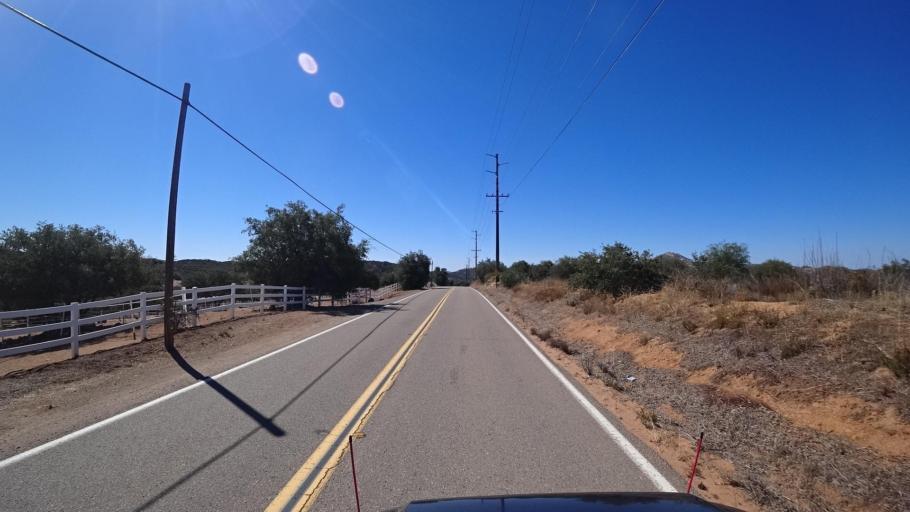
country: US
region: California
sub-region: San Diego County
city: Descanso
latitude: 32.7779
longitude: -116.6670
